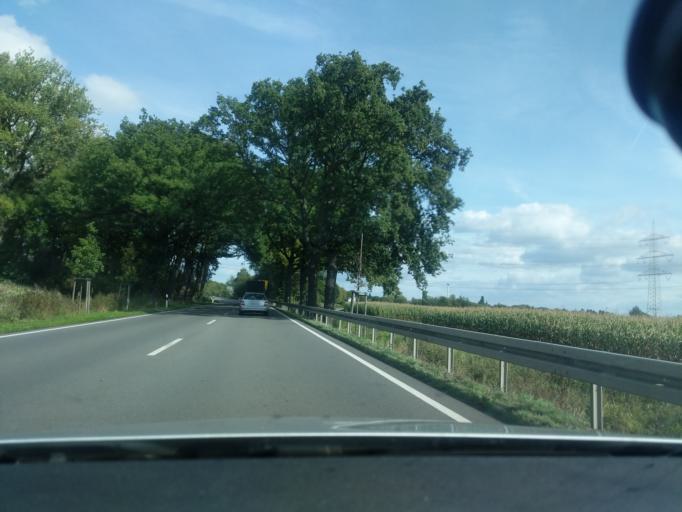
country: DE
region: Lower Saxony
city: Bohmte
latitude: 52.3552
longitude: 8.2953
